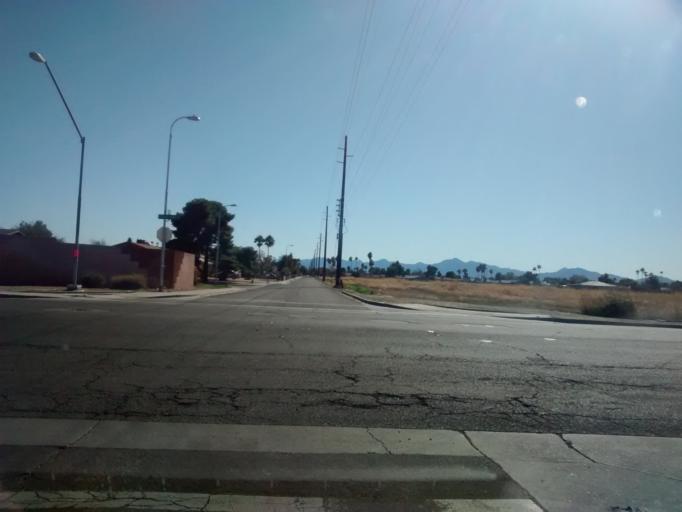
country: US
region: Arizona
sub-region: Maricopa County
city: Glendale
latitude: 33.5241
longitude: -112.2118
